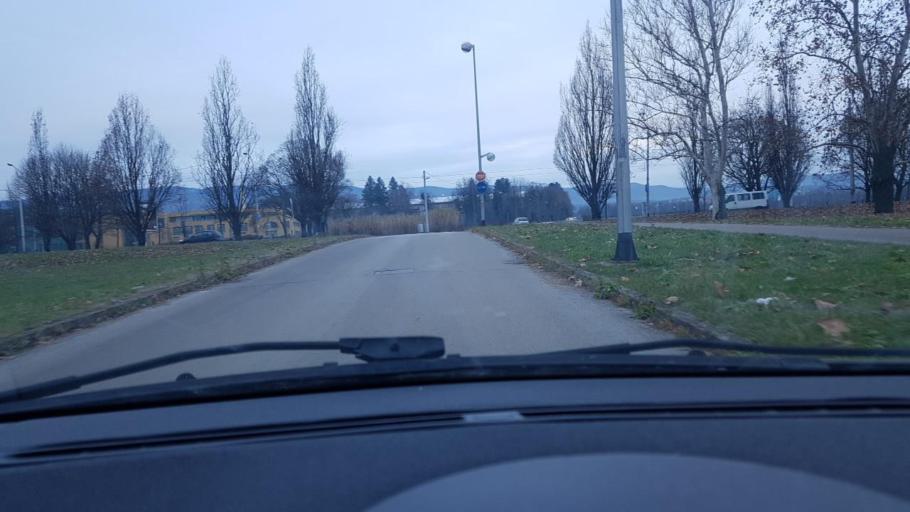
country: HR
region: Grad Zagreb
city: Dubrava
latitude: 45.8225
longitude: 16.0325
